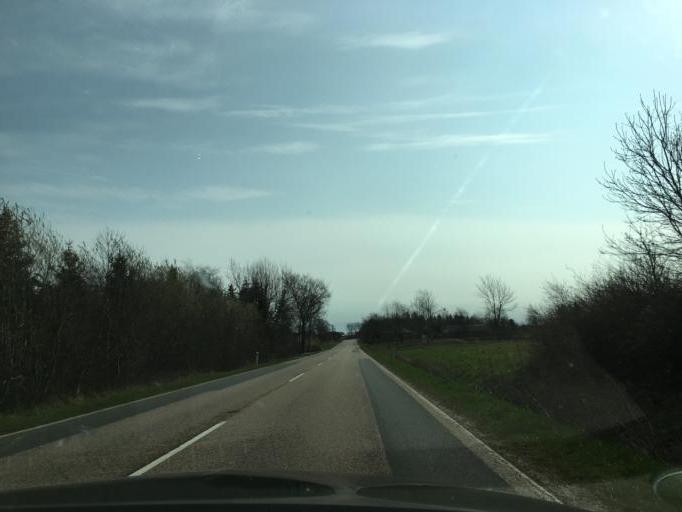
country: DK
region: South Denmark
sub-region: Vejen Kommune
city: Vejen
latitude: 55.4914
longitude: 9.1186
